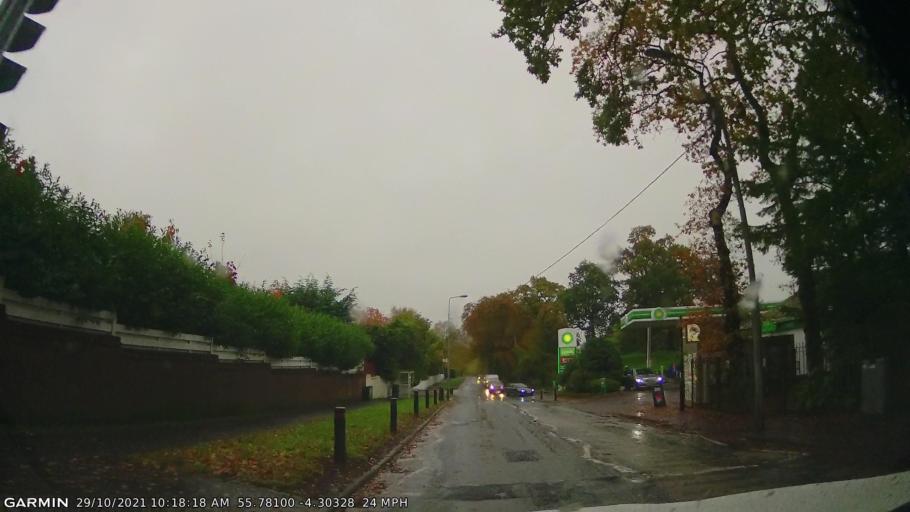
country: GB
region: Scotland
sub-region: East Renfrewshire
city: Giffnock
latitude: 55.7812
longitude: -4.3031
